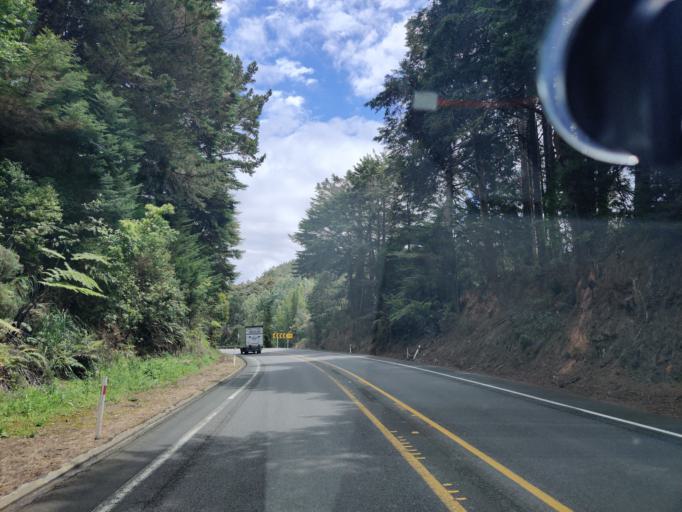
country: NZ
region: Auckland
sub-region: Auckland
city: Warkworth
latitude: -36.5037
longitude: 174.6693
